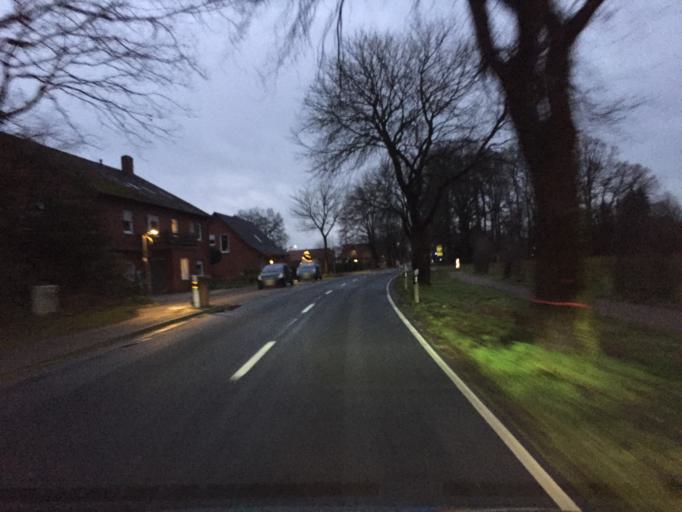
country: DE
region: Lower Saxony
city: Schwaforden
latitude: 52.7399
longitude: 8.8188
